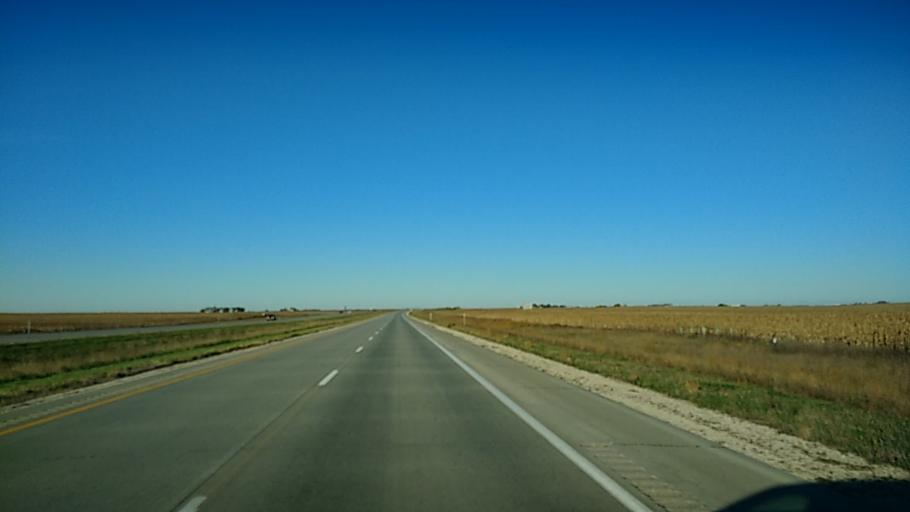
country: US
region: Iowa
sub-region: Calhoun County
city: Rockwell City
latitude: 42.4491
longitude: -94.7500
